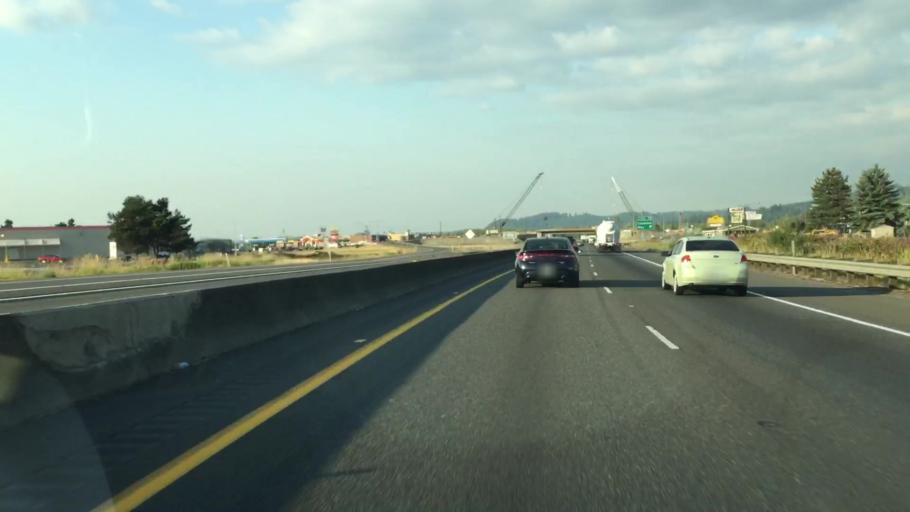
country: US
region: Washington
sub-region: Lewis County
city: Chehalis
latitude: 46.6723
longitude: -122.9769
